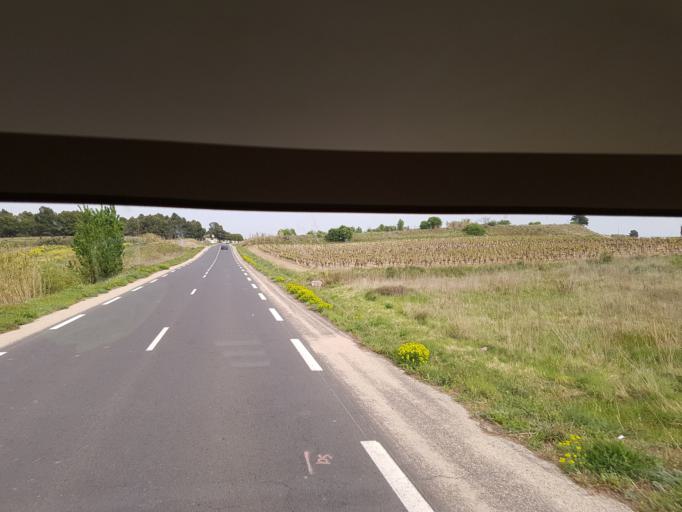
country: FR
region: Languedoc-Roussillon
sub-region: Departement de l'Herault
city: Lespignan
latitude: 43.2759
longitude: 3.1947
